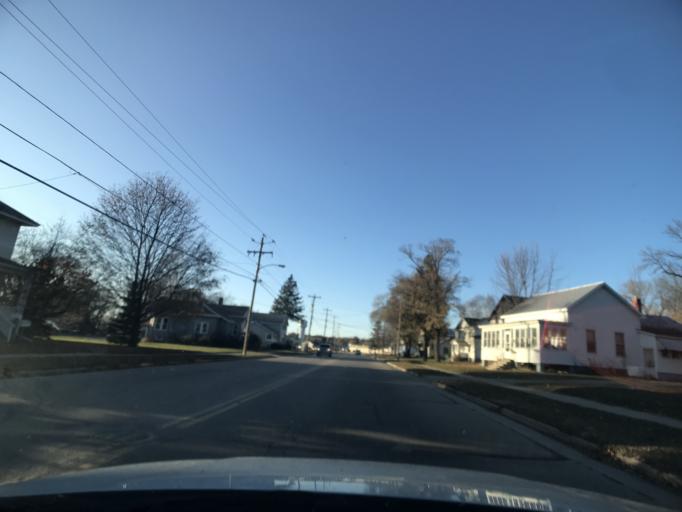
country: US
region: Wisconsin
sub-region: Oconto County
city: Oconto
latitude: 44.8920
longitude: -87.8804
